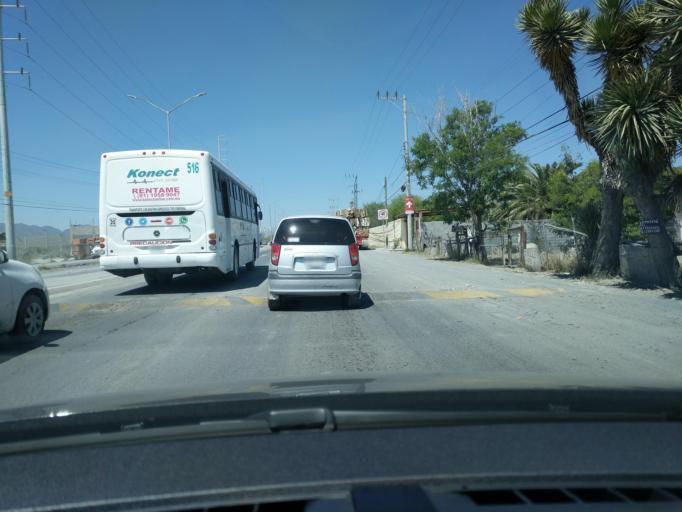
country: MX
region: Nuevo Leon
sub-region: Salinas Victoria
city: Emiliano Zapata
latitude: 25.9086
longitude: -100.2659
